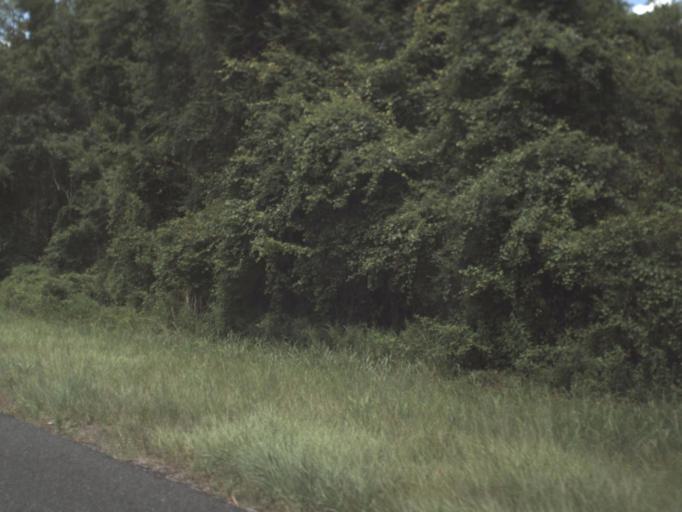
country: US
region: Florida
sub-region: Taylor County
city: Perry
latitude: 30.2080
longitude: -83.6617
